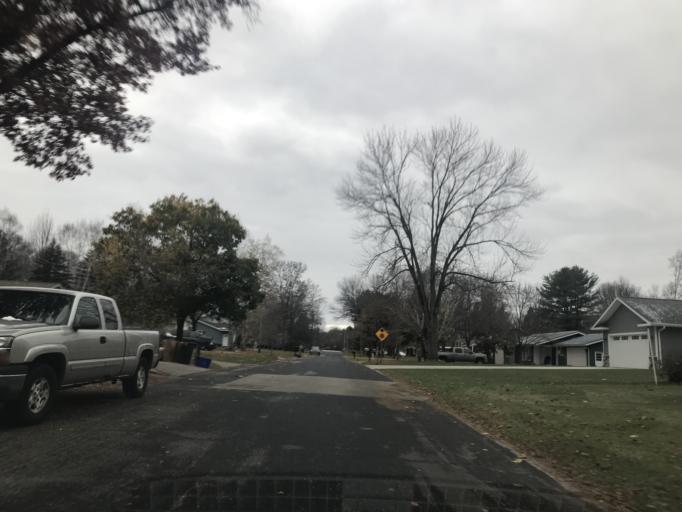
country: US
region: Wisconsin
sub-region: Marinette County
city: Marinette
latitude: 45.0976
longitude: -87.6566
